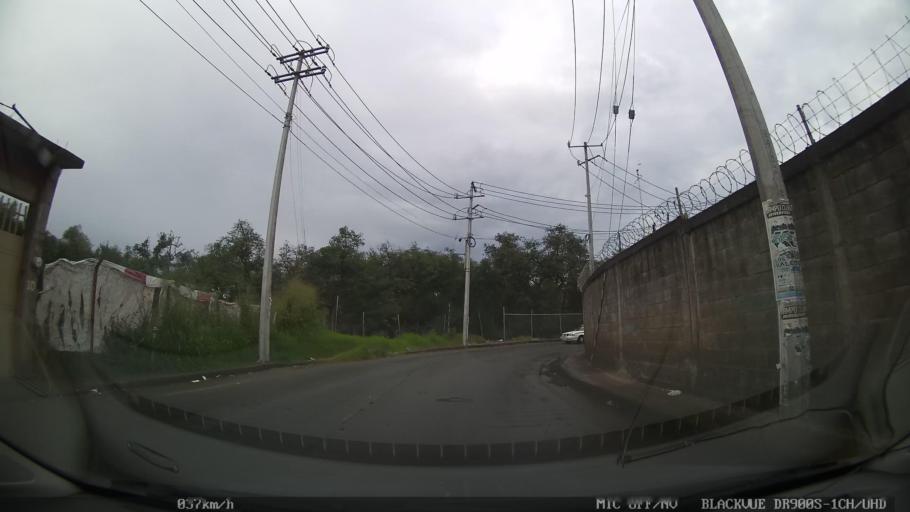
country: MX
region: Michoacan
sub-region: Uruapan
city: Santa Rosa (Santa Barbara)
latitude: 19.3847
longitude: -102.0495
